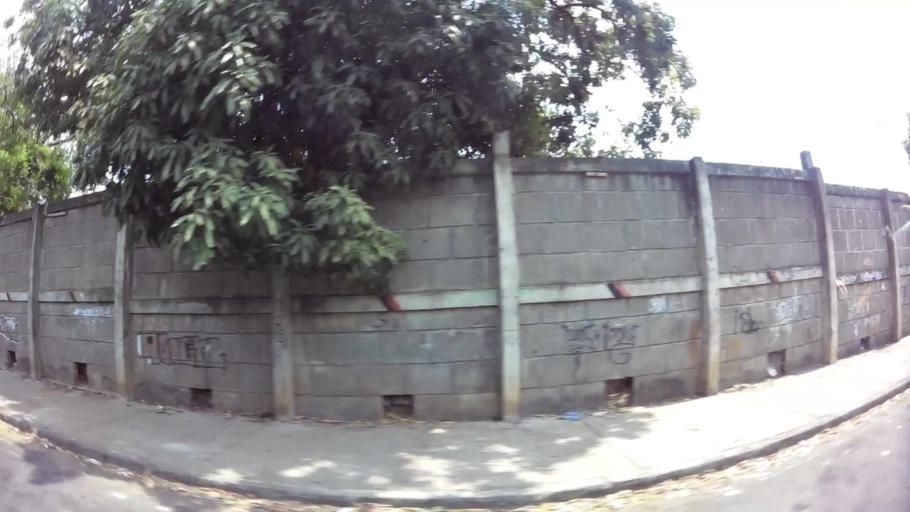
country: NI
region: Managua
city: Managua
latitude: 12.1532
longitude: -86.2924
